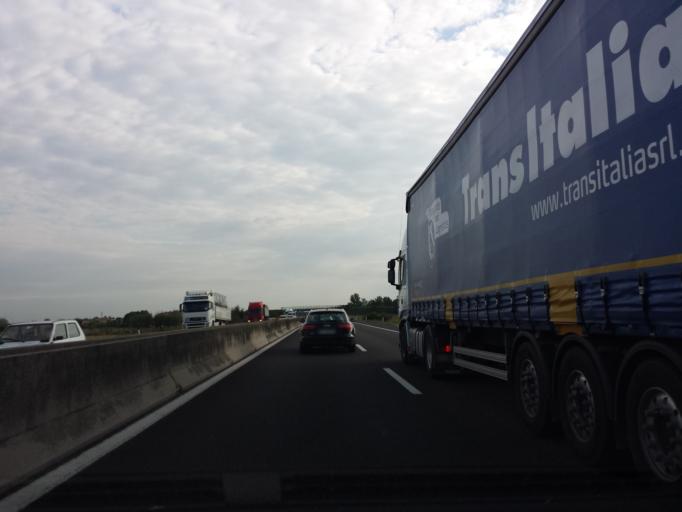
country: IT
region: Veneto
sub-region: Provincia di Padova
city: Monselice
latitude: 45.2185
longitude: 11.7746
